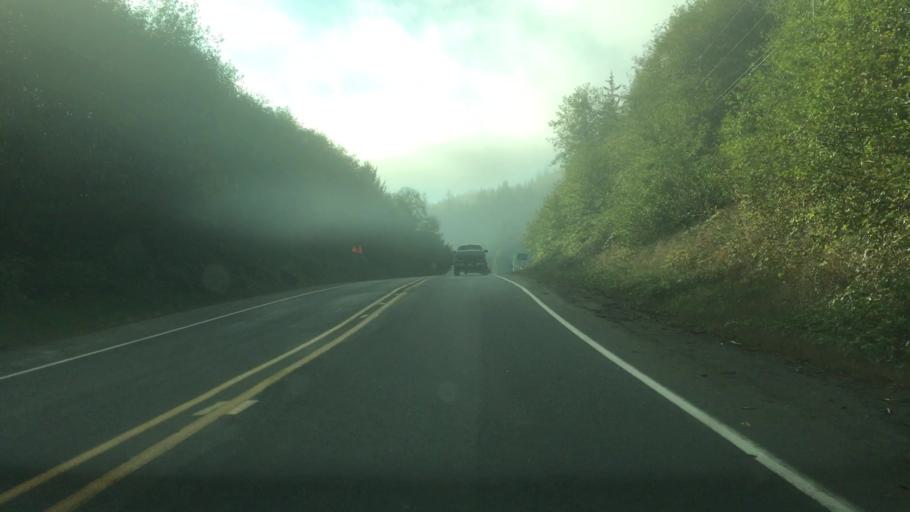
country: US
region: Oregon
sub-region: Clatsop County
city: Astoria
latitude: 46.2704
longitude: -123.8262
